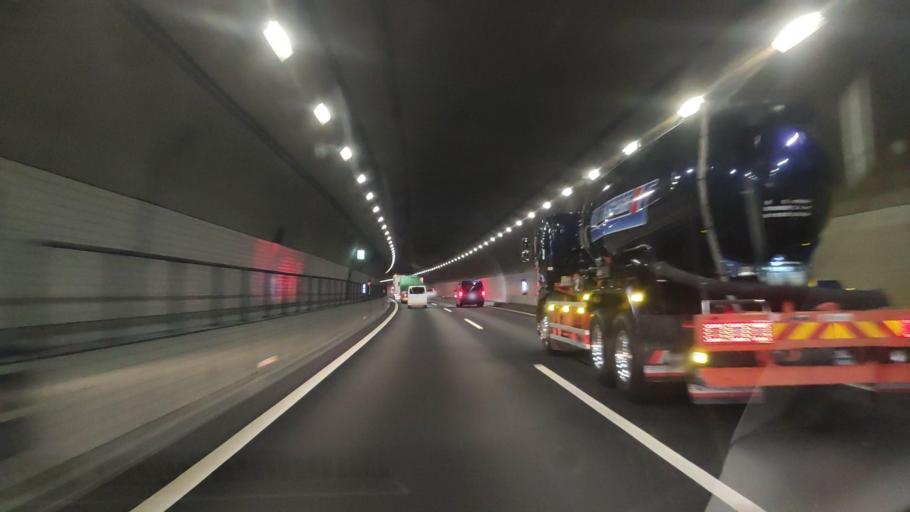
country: JP
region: Tokyo
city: Hachioji
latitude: 35.5999
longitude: 139.2708
